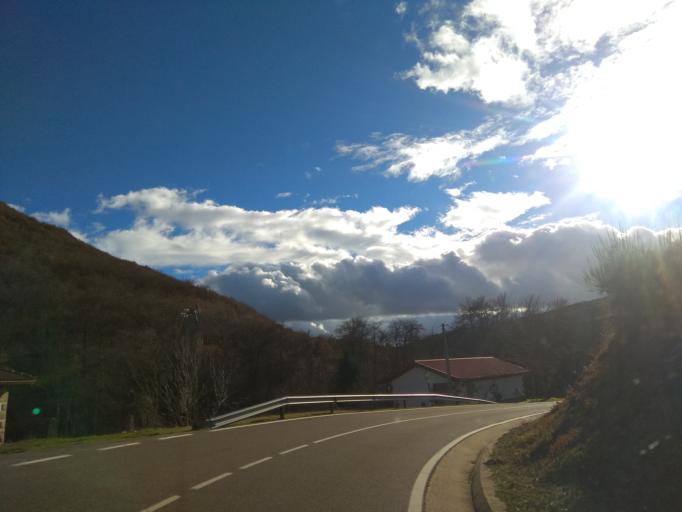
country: ES
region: Cantabria
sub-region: Provincia de Cantabria
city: San Martin de Elines
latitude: 42.8589
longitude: -3.9127
